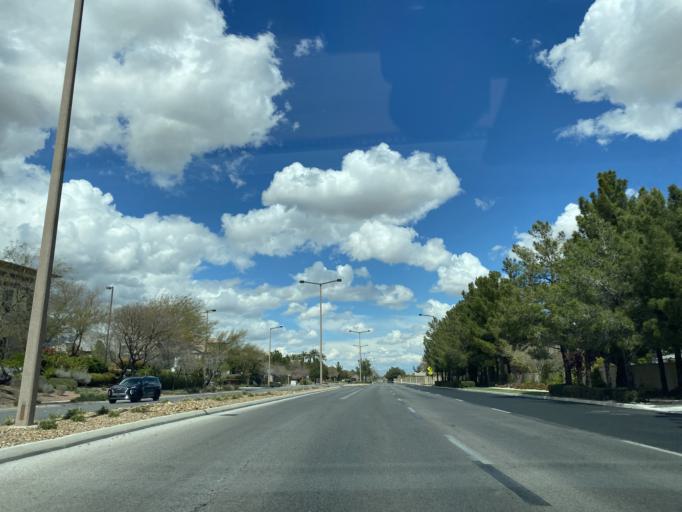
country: US
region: Nevada
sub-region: Clark County
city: Summerlin South
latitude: 36.1602
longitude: -115.3141
